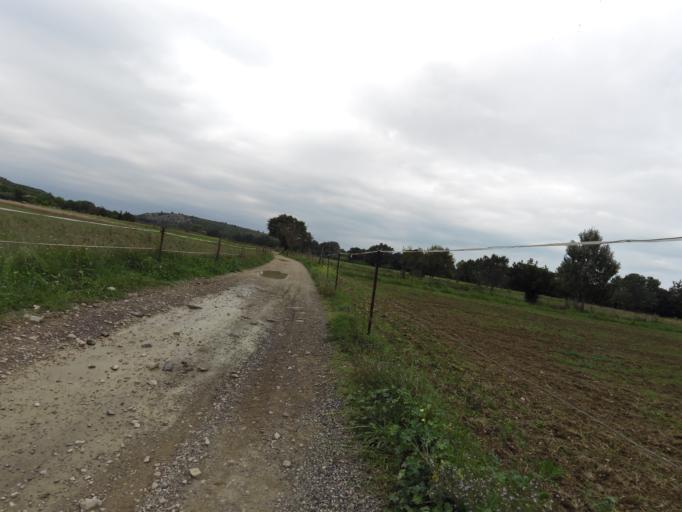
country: FR
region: Languedoc-Roussillon
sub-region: Departement de l'Herault
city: Villetelle
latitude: 43.7376
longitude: 4.1381
